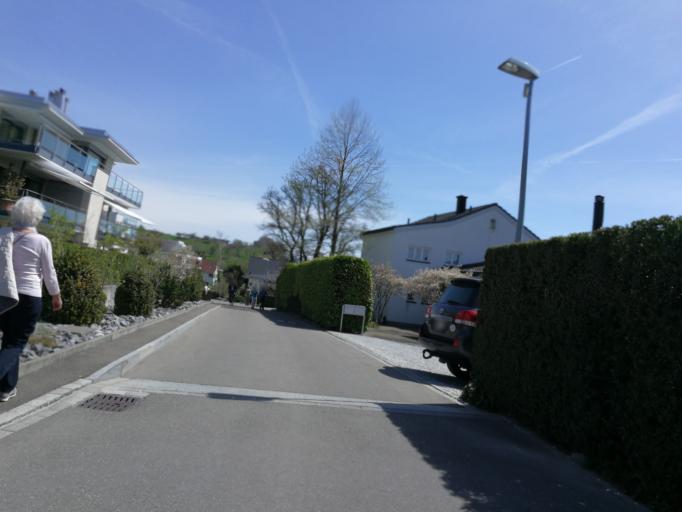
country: CH
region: Zurich
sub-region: Bezirk Meilen
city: Feldmeilen
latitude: 47.2793
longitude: 8.6241
